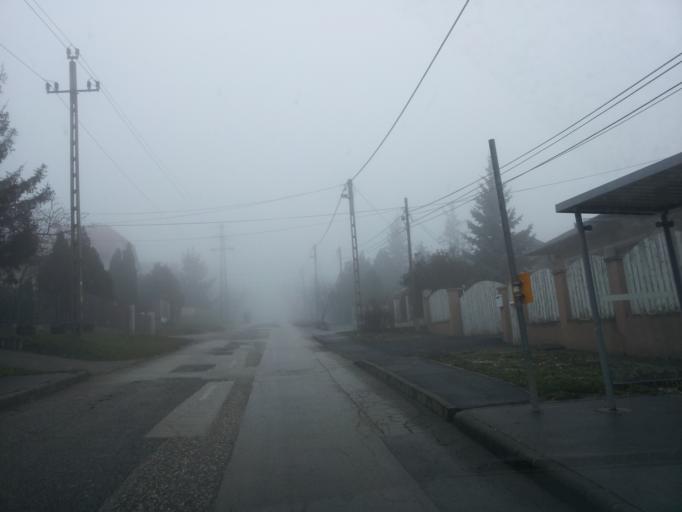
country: HU
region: Pest
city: Toeroekbalint
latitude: 47.4185
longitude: 18.8905
